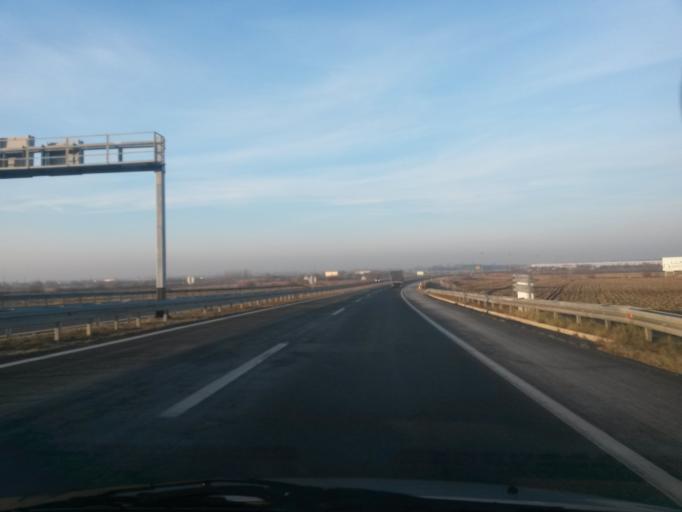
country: HR
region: Varazdinska
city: Jalzabet
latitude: 46.2516
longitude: 16.3997
